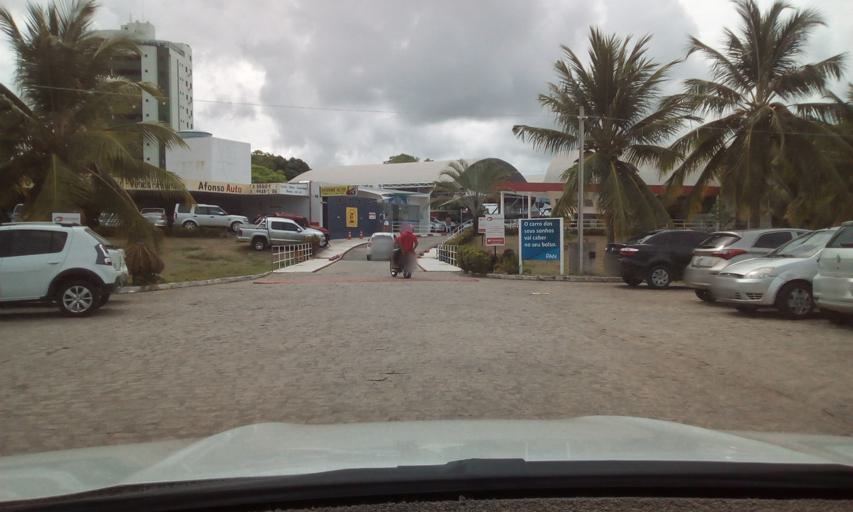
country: BR
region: Paraiba
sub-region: Joao Pessoa
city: Joao Pessoa
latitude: -7.0942
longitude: -34.8462
